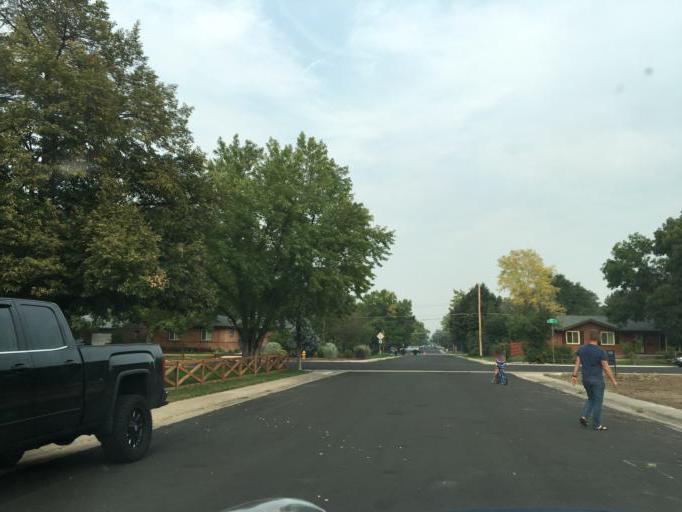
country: US
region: Colorado
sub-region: Arapahoe County
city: Glendale
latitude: 39.6875
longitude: -104.9300
